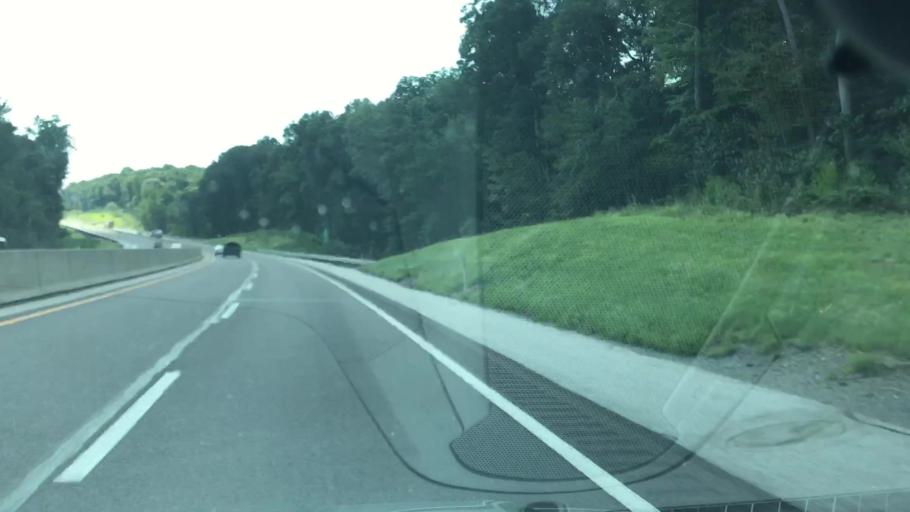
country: US
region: Pennsylvania
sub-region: Lebanon County
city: Cornwall
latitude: 40.2279
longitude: -76.4891
